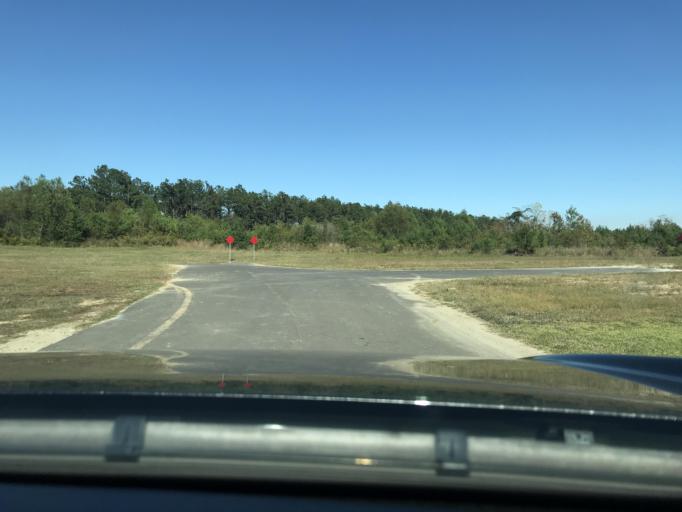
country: US
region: Louisiana
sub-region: Calcasieu Parish
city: Moss Bluff
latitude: 30.3130
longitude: -93.2559
